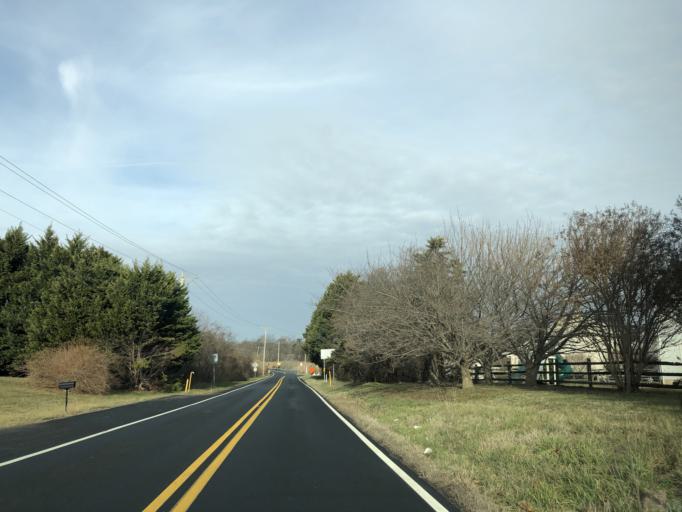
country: US
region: Delaware
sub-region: New Castle County
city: Middletown
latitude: 39.4490
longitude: -75.6487
